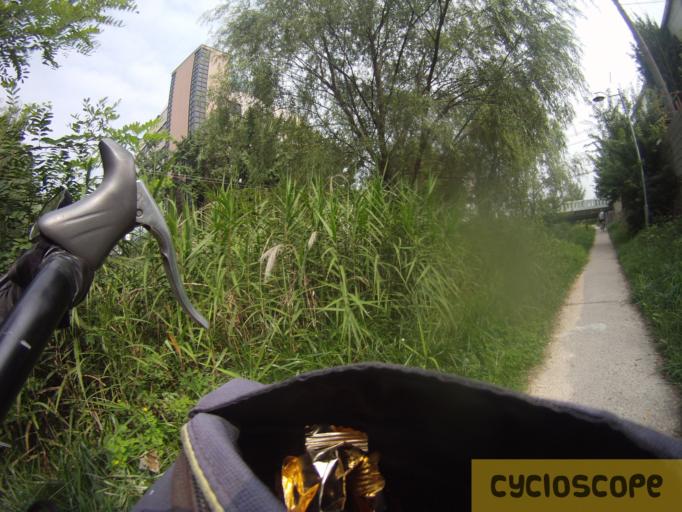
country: KR
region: Gyeonggi-do
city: Suwon-si
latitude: 37.3459
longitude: 126.9740
